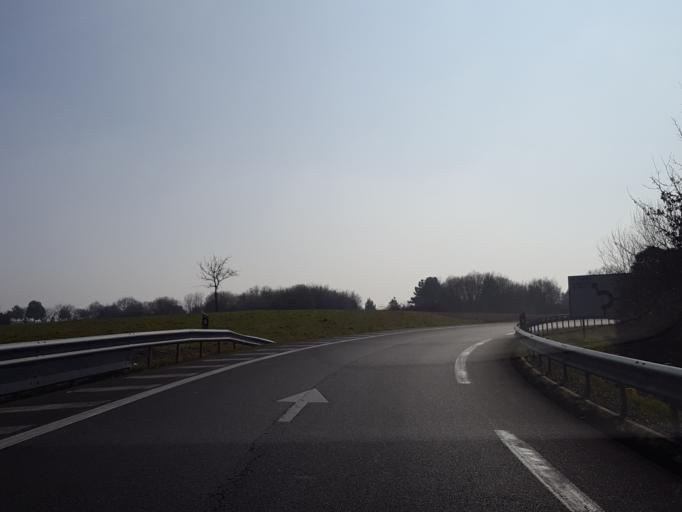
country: FR
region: Pays de la Loire
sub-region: Departement de la Vendee
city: La Chaize-le-Vicomte
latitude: 46.6694
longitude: -1.3162
